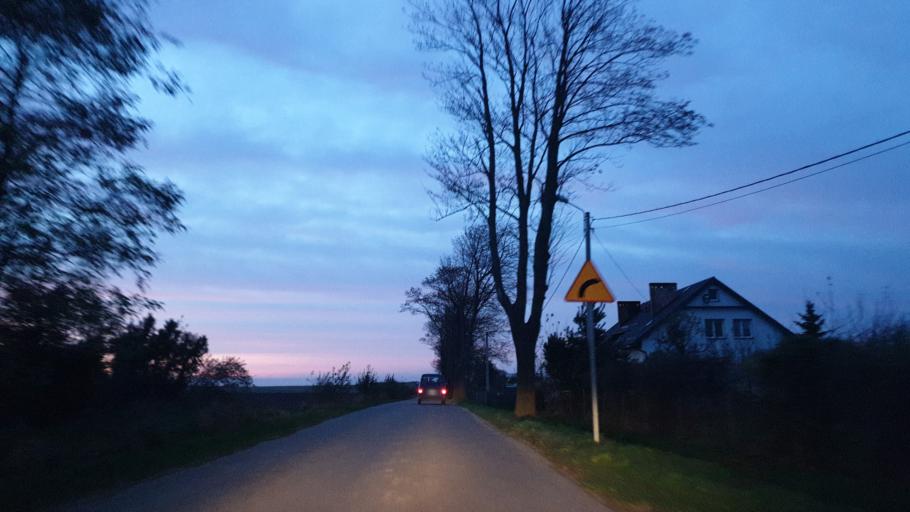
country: PL
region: Pomeranian Voivodeship
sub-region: Powiat pucki
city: Krokowa
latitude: 54.7773
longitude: 18.2068
